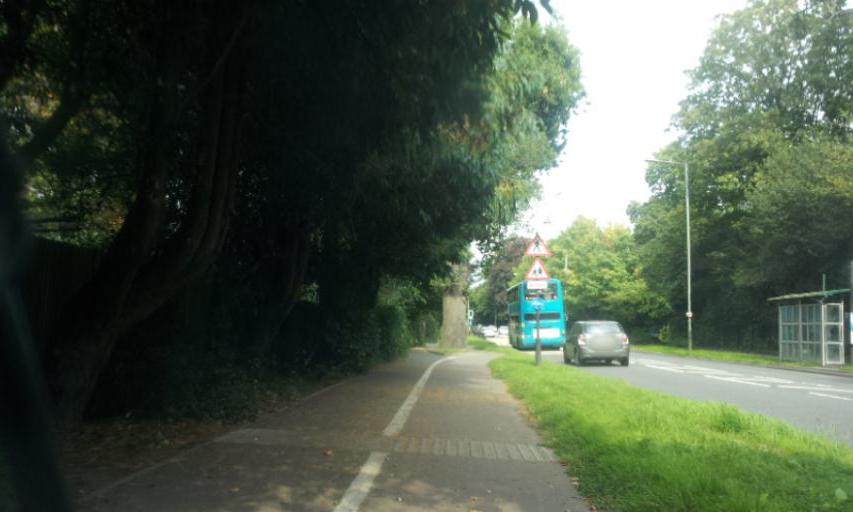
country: GB
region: England
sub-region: Kent
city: Royal Tunbridge Wells
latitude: 51.1355
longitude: 0.2838
